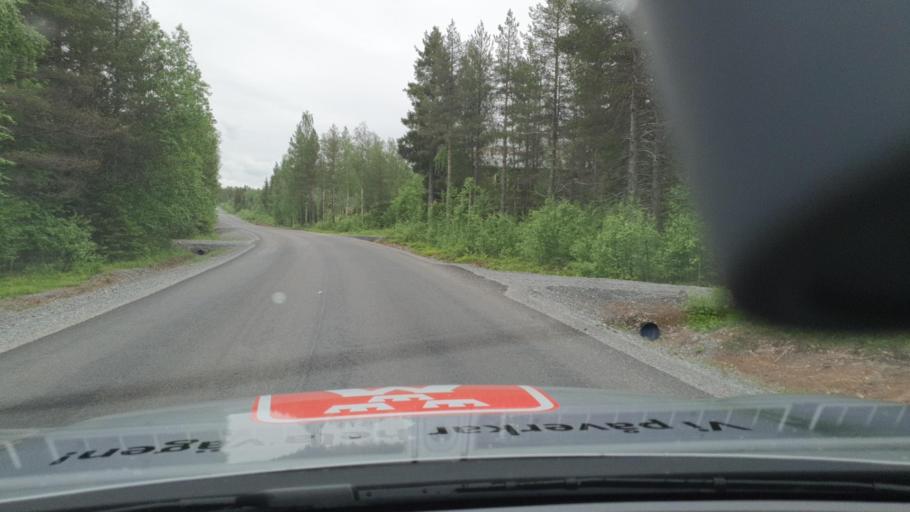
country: SE
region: Norrbotten
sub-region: Overtornea Kommun
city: OEvertornea
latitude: 66.6096
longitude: 23.2939
